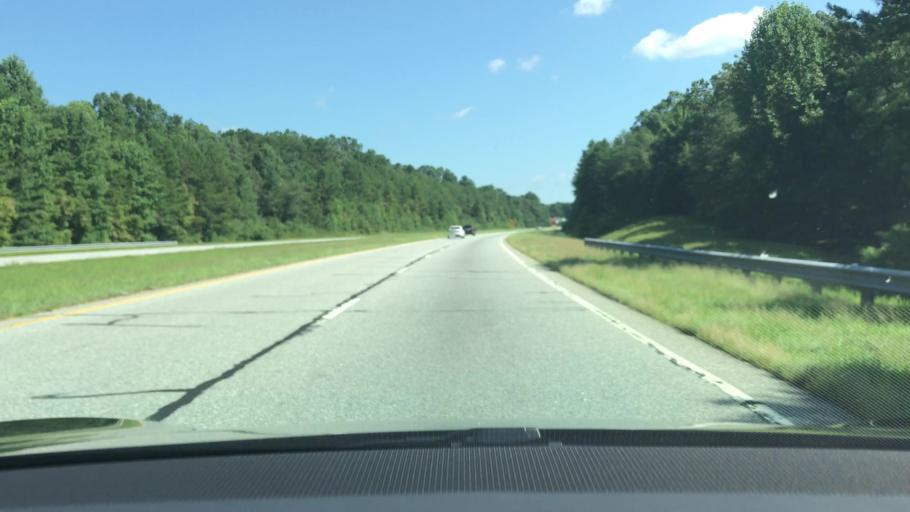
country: US
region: Georgia
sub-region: Habersham County
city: Clarkesville
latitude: 34.6405
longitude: -83.4508
